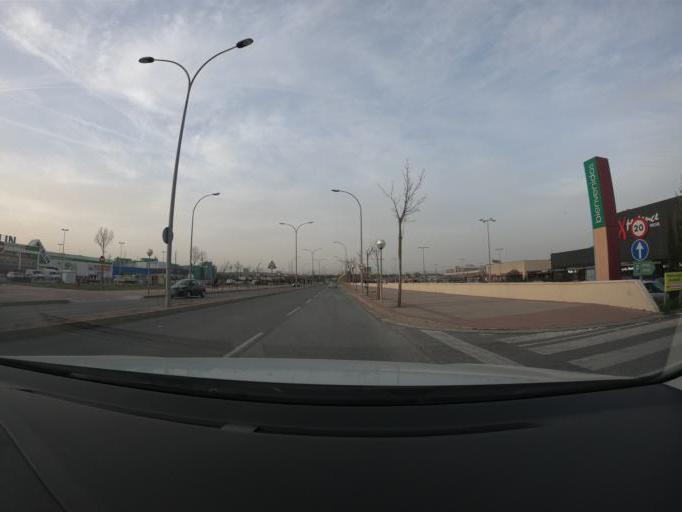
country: ES
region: La Rioja
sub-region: Provincia de La Rioja
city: Logrono
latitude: 42.4513
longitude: -2.4709
